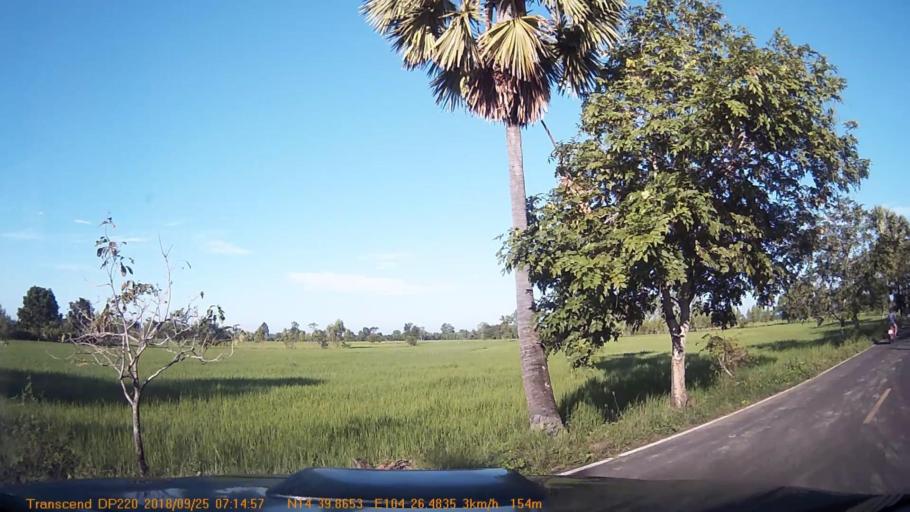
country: TH
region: Sisaket
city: Khun Han
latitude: 14.6644
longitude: 104.4415
